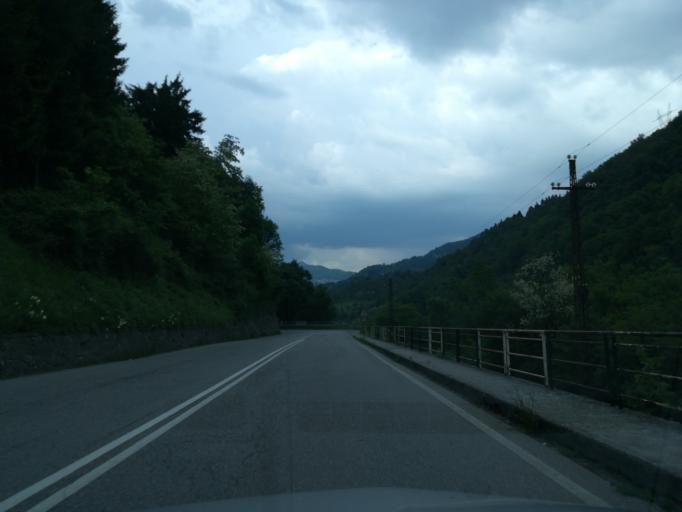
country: IT
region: Lombardy
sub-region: Provincia di Bergamo
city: Strozza
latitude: 45.7766
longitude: 9.5805
